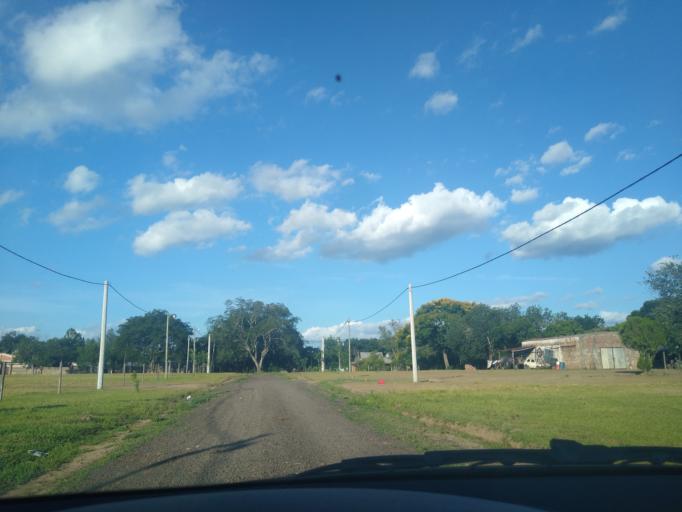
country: AR
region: Chaco
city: Resistencia
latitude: -27.4398
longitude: -58.9538
